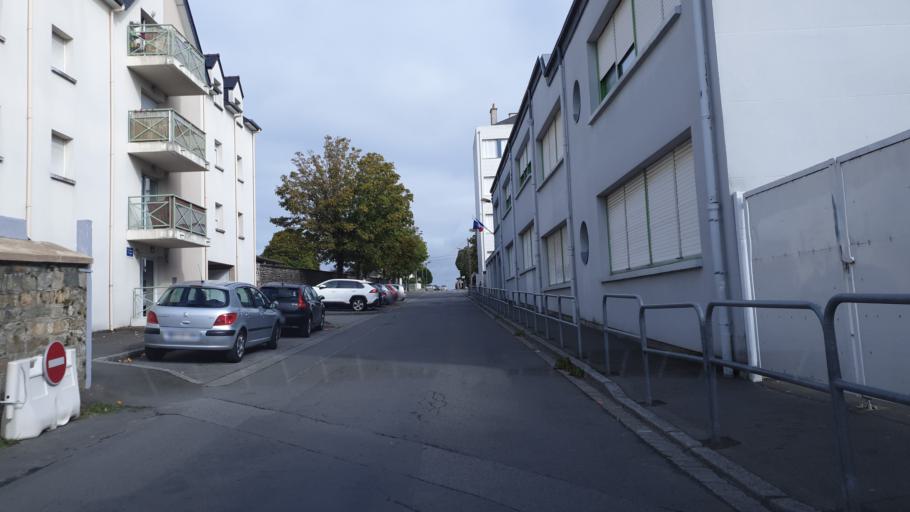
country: FR
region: Brittany
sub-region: Departement d'Ille-et-Vilaine
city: Janze
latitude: 47.9611
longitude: -1.4995
